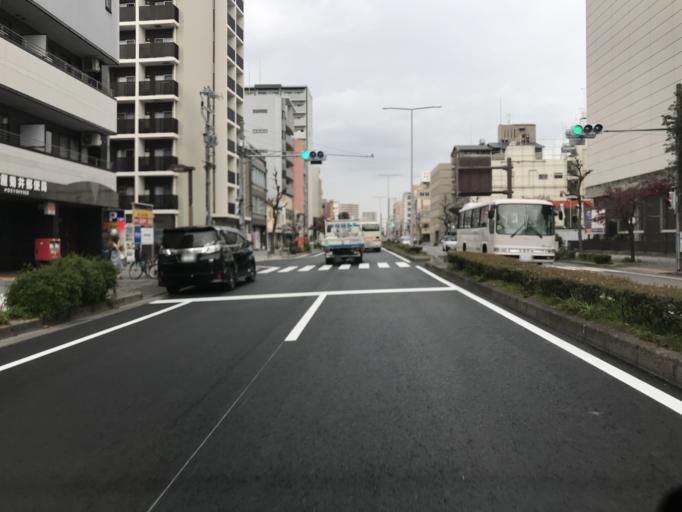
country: JP
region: Aichi
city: Nagoya-shi
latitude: 35.1789
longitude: 136.8860
